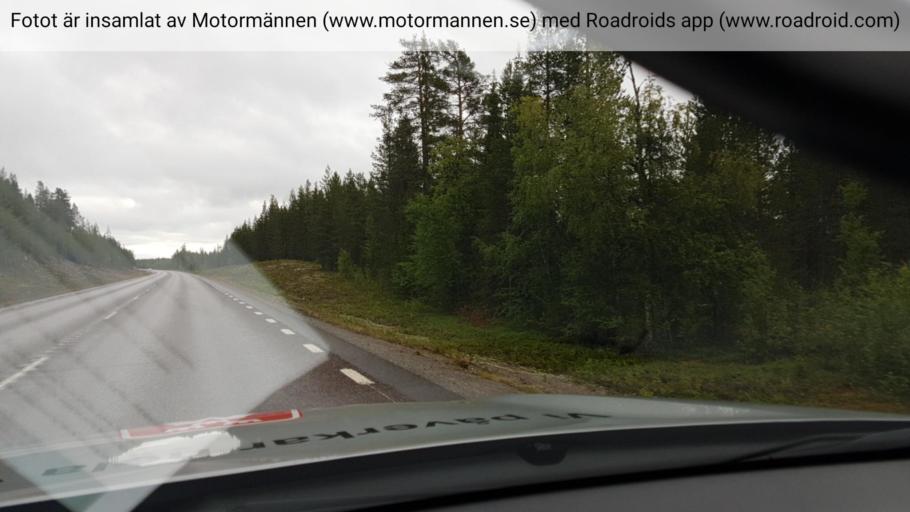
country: SE
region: Norrbotten
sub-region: Gallivare Kommun
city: Gaellivare
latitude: 67.1094
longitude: 20.8061
